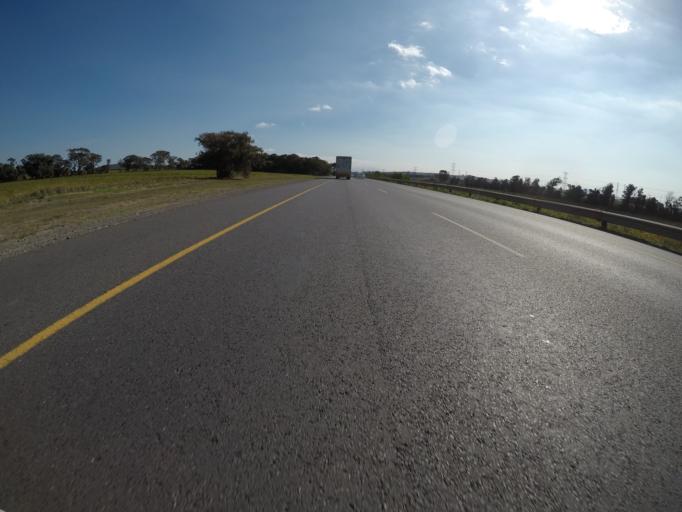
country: ZA
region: Western Cape
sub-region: City of Cape Town
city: Kraaifontein
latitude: -33.8819
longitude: 18.7583
